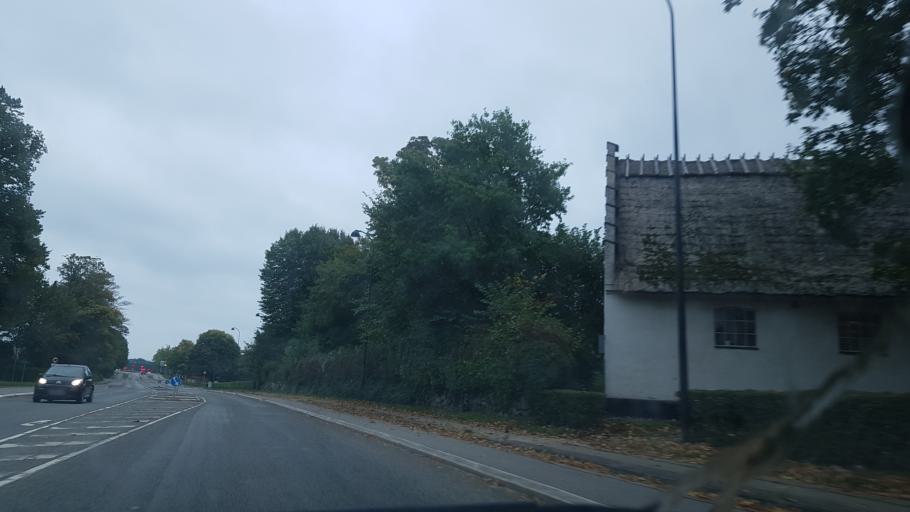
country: DK
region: Capital Region
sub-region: Rudersdal Kommune
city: Trorod
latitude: 55.8291
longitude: 12.5162
